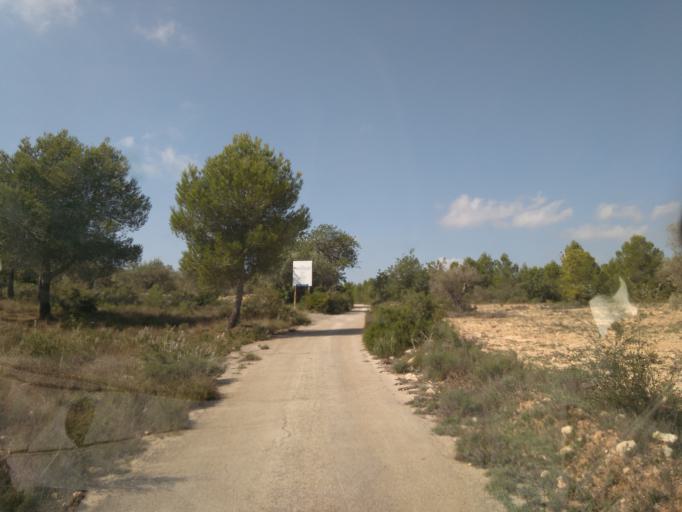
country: ES
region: Valencia
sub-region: Provincia de Valencia
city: Tous
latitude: 39.1766
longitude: -0.6187
